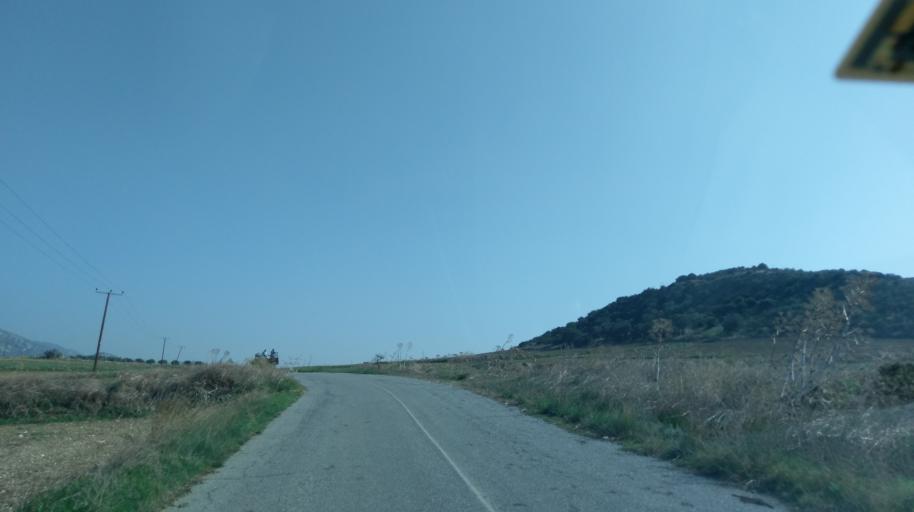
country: CY
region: Ammochostos
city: Lefkonoiko
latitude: 35.3290
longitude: 33.7047
